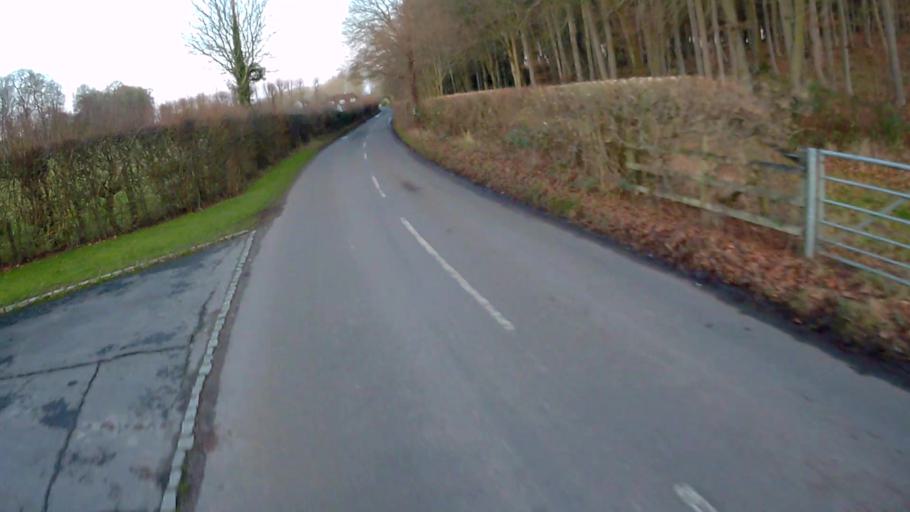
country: GB
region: England
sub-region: Hampshire
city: Overton
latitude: 51.2379
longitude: -1.2206
